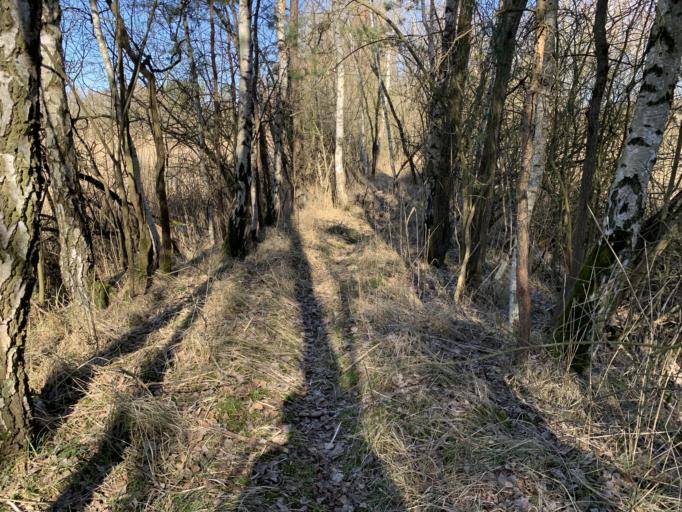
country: DE
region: Mecklenburg-Vorpommern
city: Blankensee
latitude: 53.3969
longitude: 13.2557
